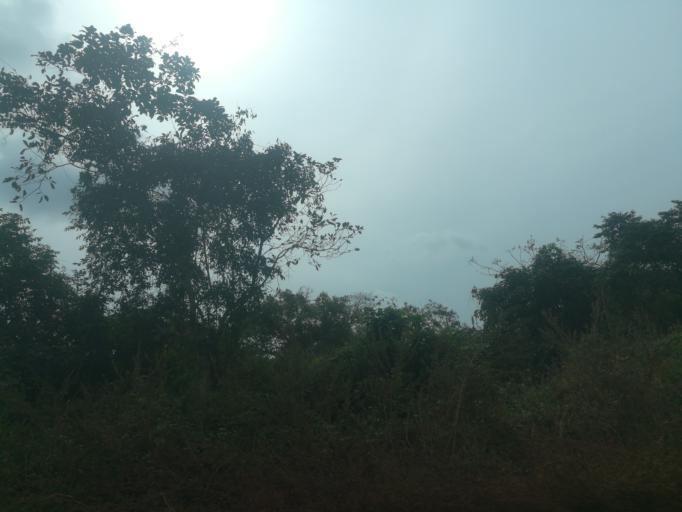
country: NG
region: Ogun
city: Ayetoro
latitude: 7.2929
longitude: 3.0790
